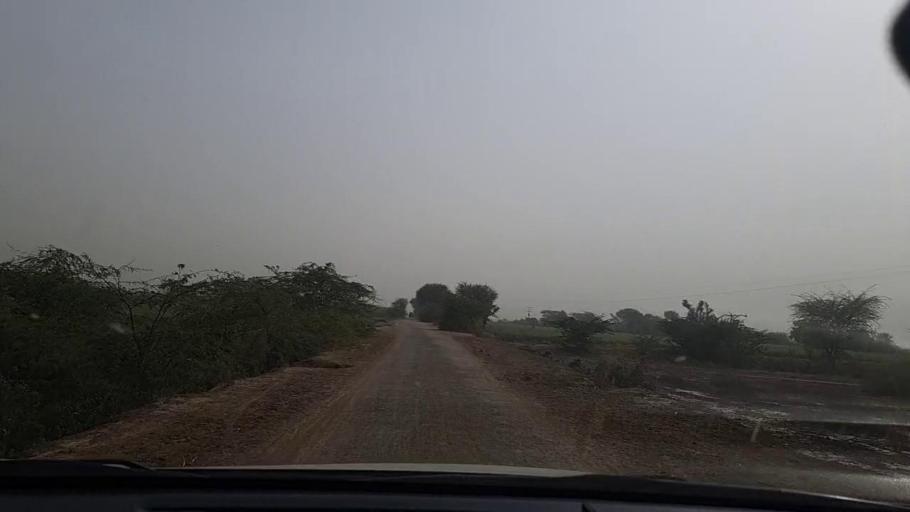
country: PK
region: Sindh
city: Pithoro
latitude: 25.4266
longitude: 69.3160
